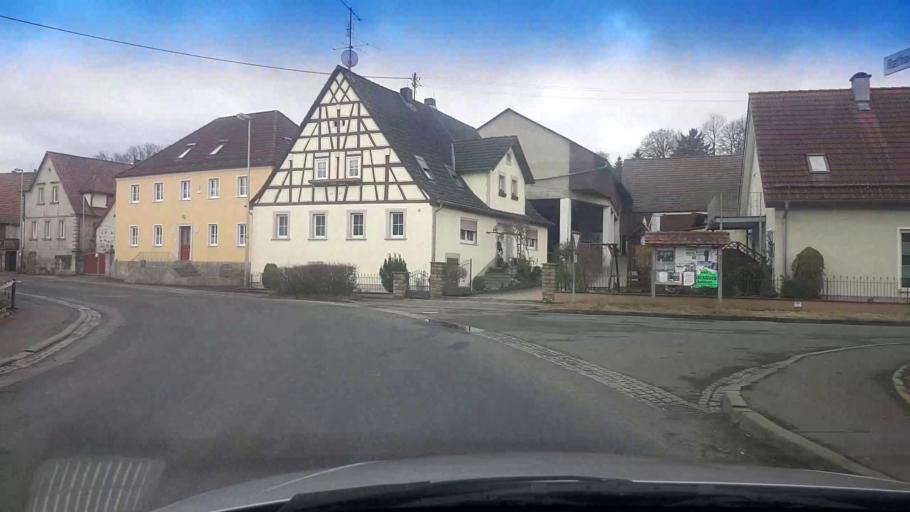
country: DE
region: Bavaria
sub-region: Regierungsbezirk Unterfranken
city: Eltmann
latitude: 49.9302
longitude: 10.6523
